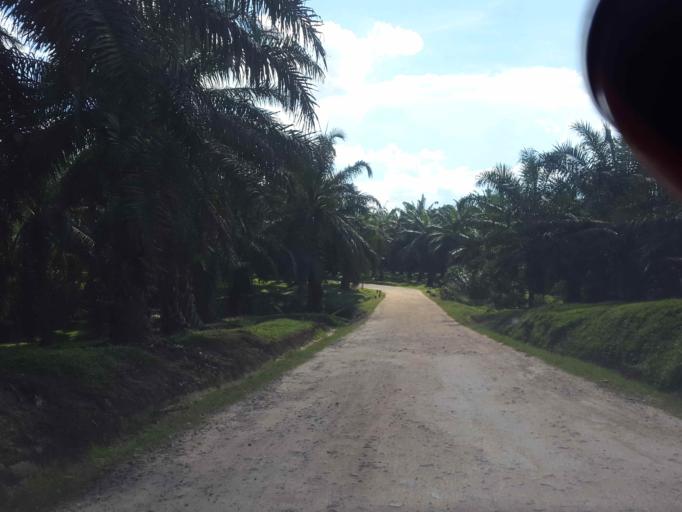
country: ID
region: Lampung
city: Natar
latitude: -5.2962
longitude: 105.1712
